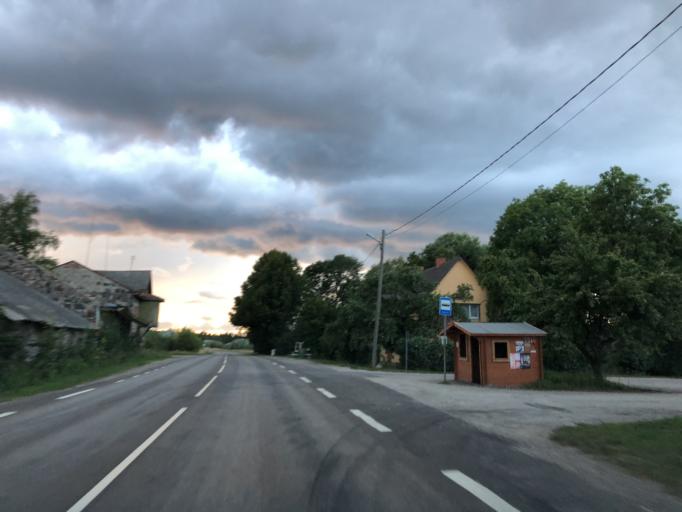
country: EE
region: Laeaene
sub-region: Ridala Parish
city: Uuemoisa
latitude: 58.8672
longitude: 23.6220
